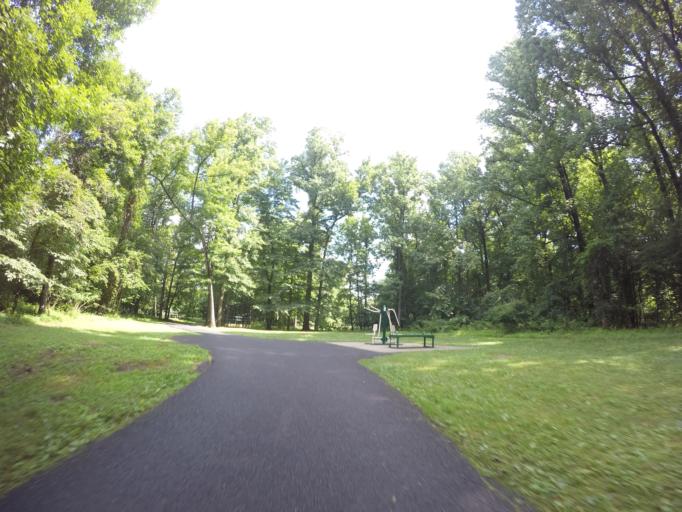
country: US
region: Maryland
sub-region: Prince George's County
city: East Riverdale
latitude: 38.9721
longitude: -76.9199
